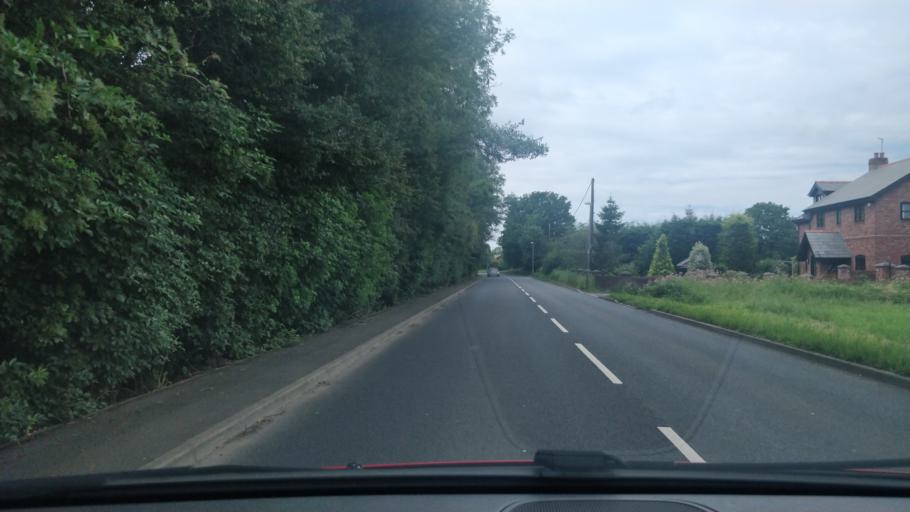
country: GB
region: England
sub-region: Lancashire
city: Leyland
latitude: 53.7033
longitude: -2.7325
